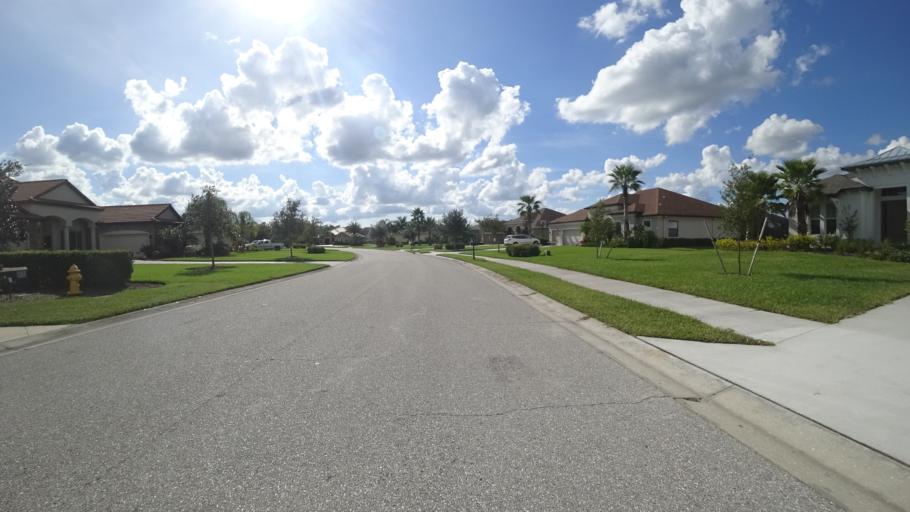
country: US
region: Florida
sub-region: Manatee County
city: Ellenton
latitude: 27.5424
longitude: -82.3788
